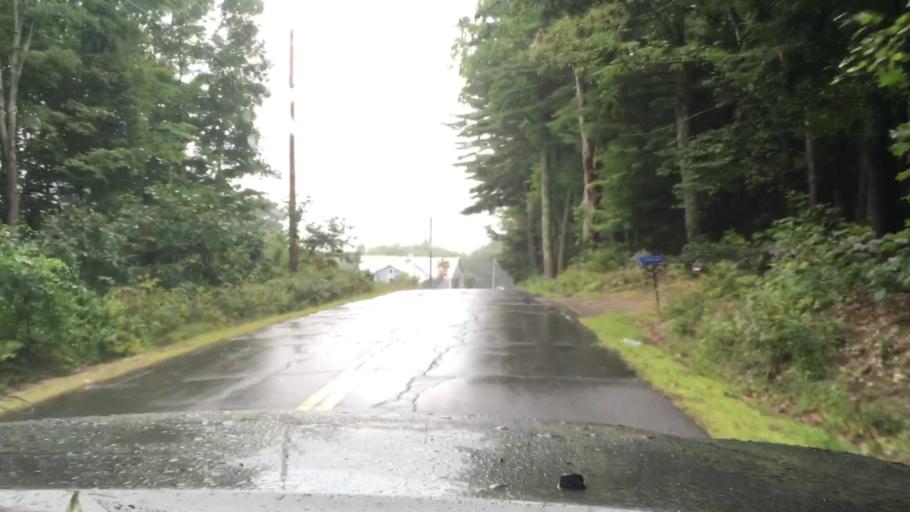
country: US
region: New Hampshire
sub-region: Belknap County
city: Meredith
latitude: 43.6739
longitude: -71.5272
